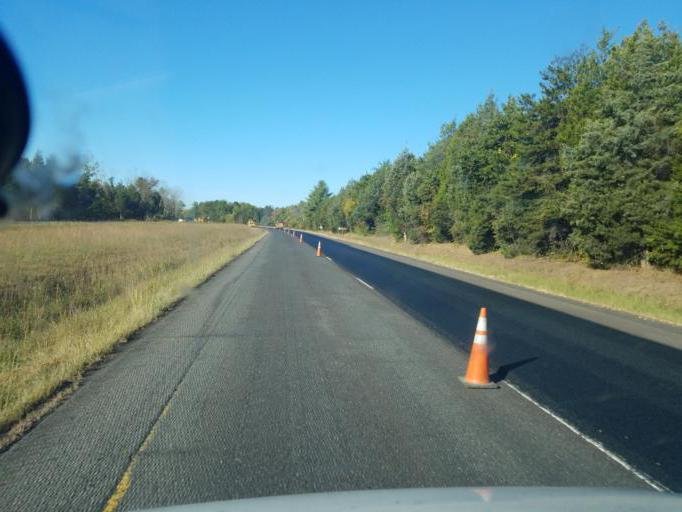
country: US
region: Virginia
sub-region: Fauquier County
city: Bealeton
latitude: 38.5241
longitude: -77.8292
